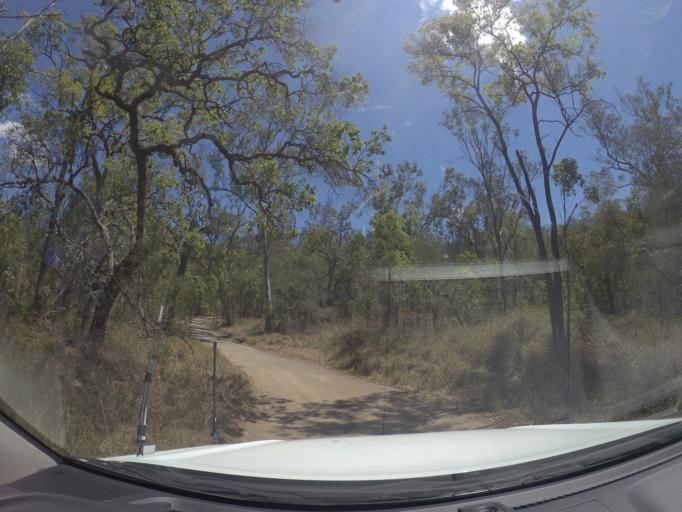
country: AU
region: Queensland
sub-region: Ipswich
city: Springfield Lakes
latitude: -27.8065
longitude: 152.8448
